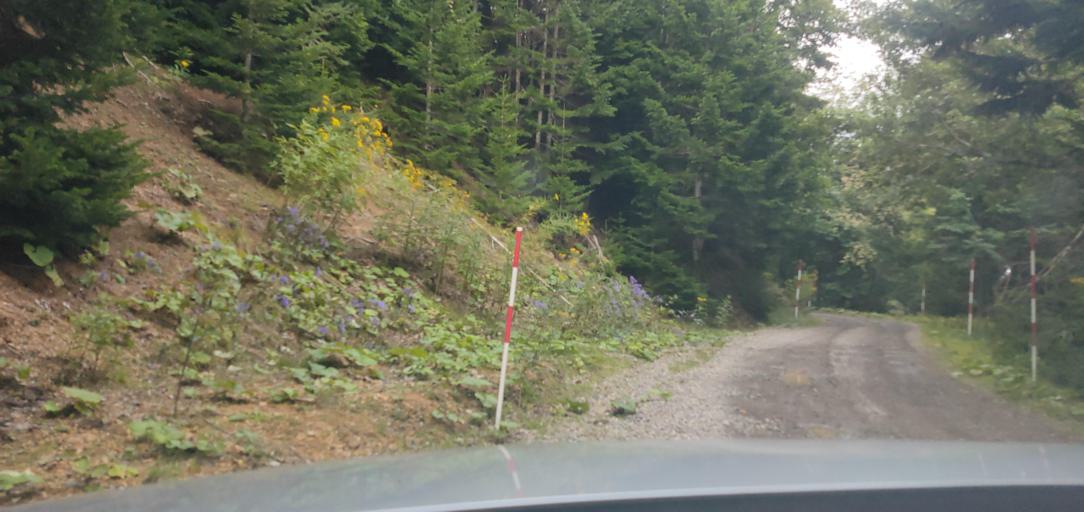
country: JP
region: Hokkaido
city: Kitami
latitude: 43.3700
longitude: 143.9436
